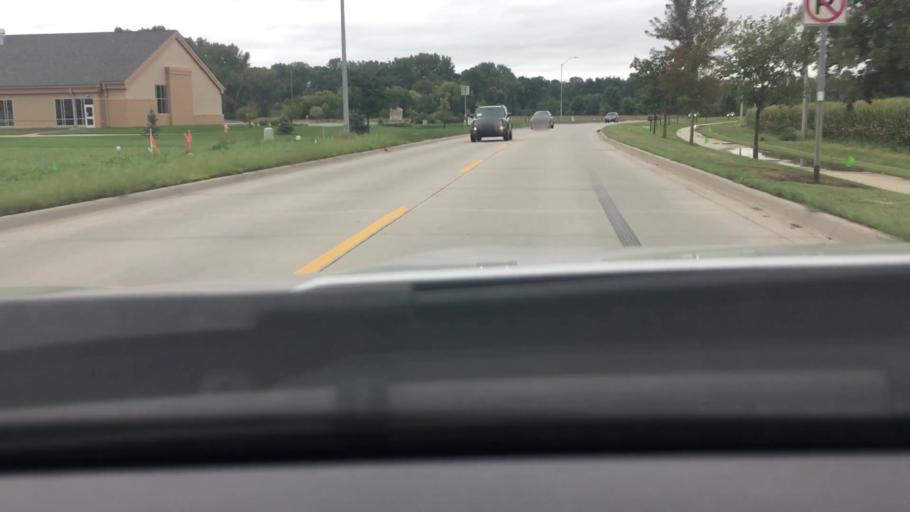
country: US
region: Iowa
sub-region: Pottawattamie County
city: Council Bluffs
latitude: 41.2652
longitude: -95.8039
